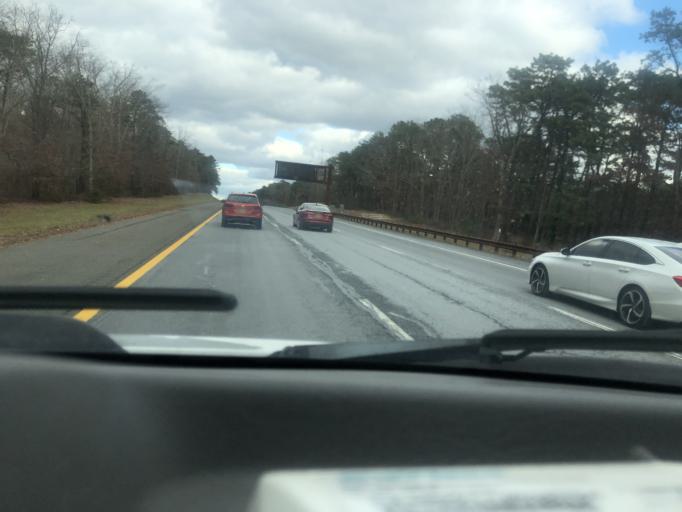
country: US
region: New Jersey
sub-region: Ocean County
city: Ocean Acres
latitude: 39.7187
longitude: -74.2732
